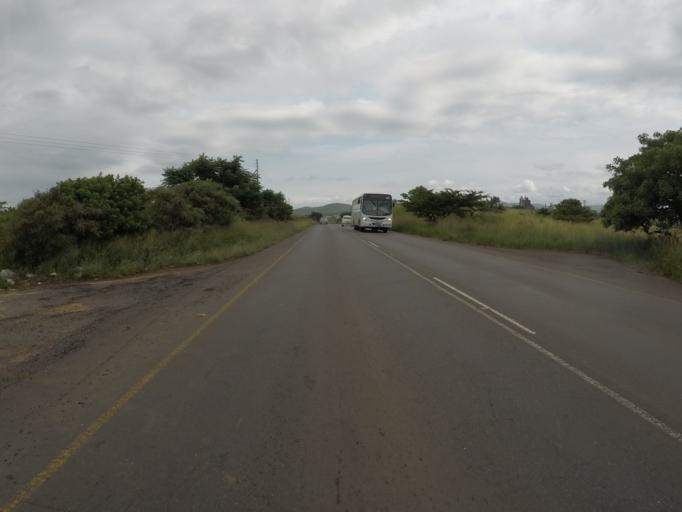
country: ZA
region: KwaZulu-Natal
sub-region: uThungulu District Municipality
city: Empangeni
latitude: -28.7316
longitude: 31.8736
